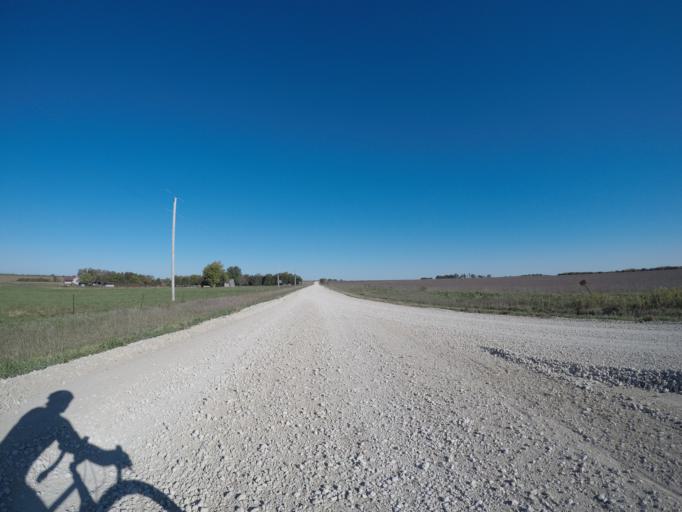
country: US
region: Kansas
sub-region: Morris County
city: Council Grove
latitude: 38.8412
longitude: -96.4089
